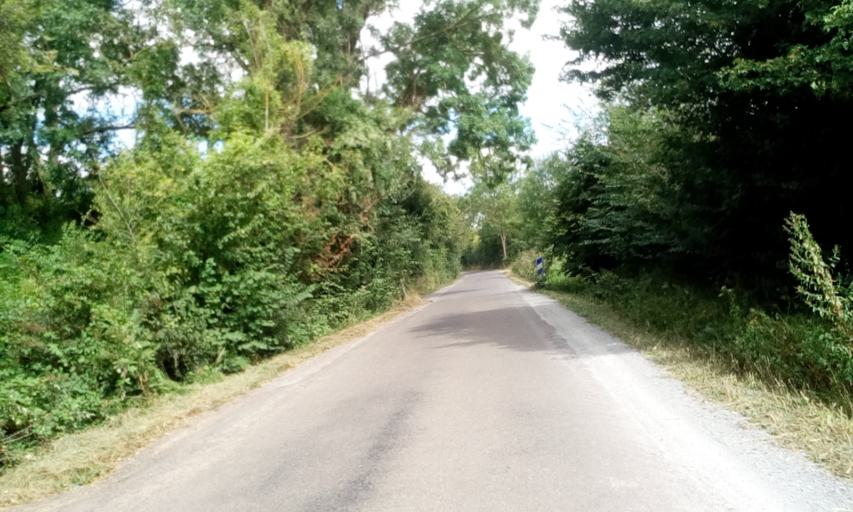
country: FR
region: Lower Normandy
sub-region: Departement du Calvados
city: Sannerville
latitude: 49.1740
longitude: -0.2040
